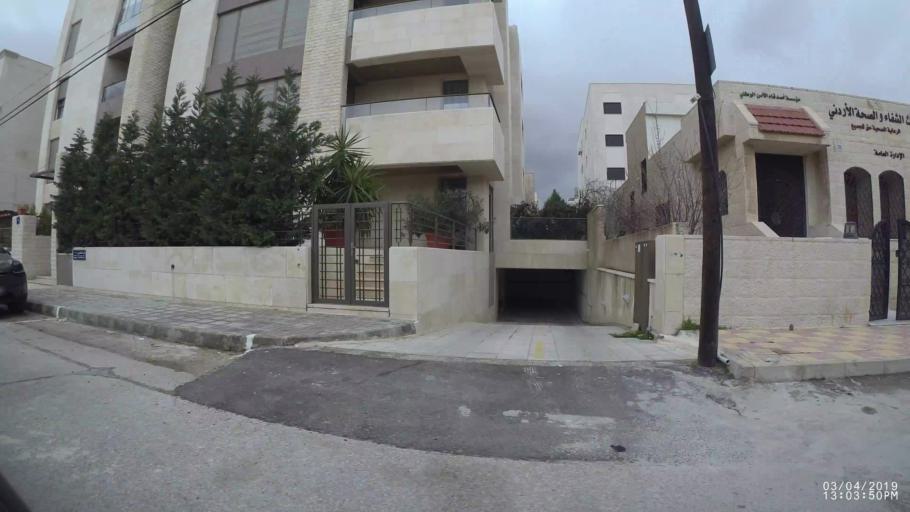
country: JO
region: Amman
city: Wadi as Sir
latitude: 31.9663
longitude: 35.8284
